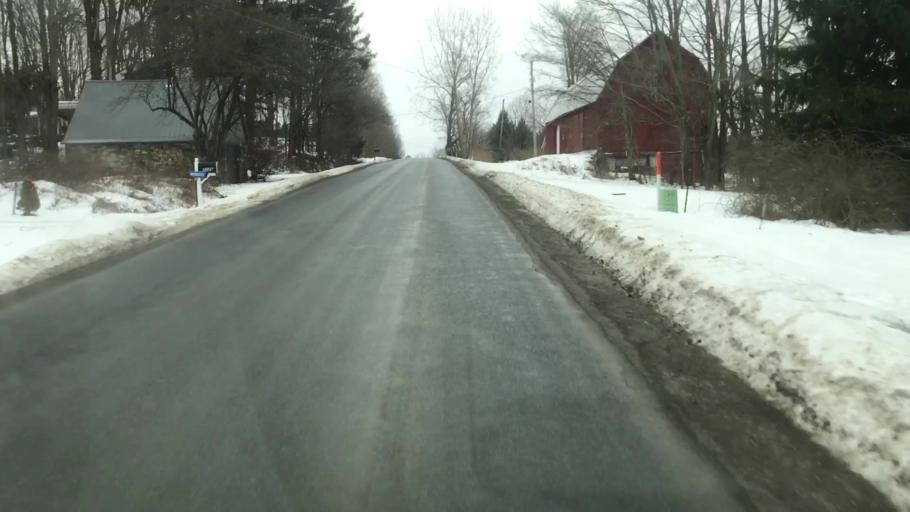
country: US
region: New York
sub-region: Cortland County
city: Cortland West
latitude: 42.6509
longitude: -76.2684
